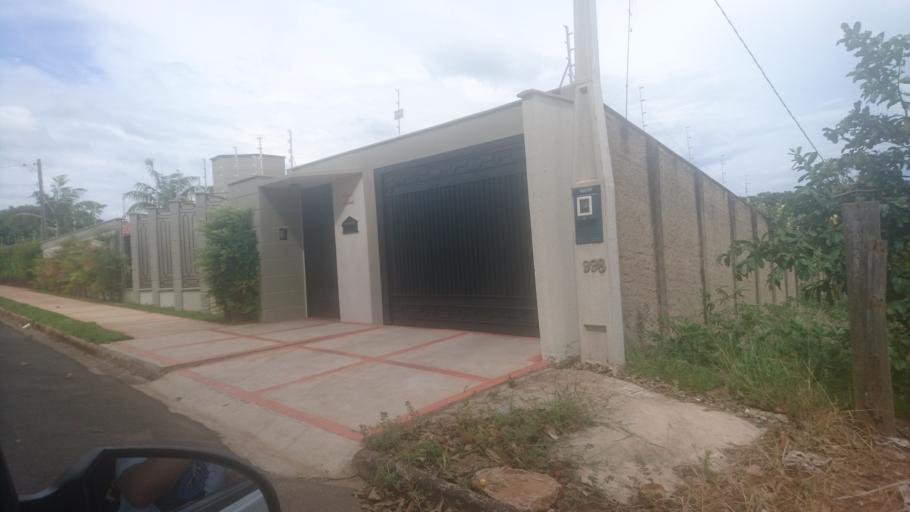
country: BR
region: Sao Paulo
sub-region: Casa Branca
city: Casa Branca
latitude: -21.7822
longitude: -47.0811
